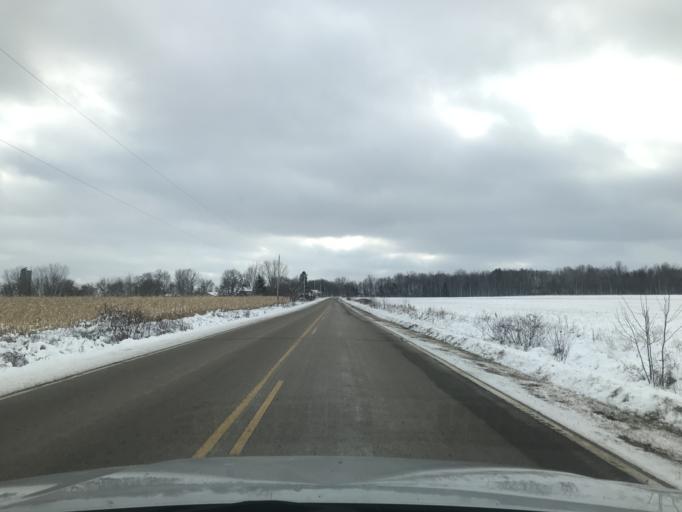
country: US
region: Wisconsin
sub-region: Oconto County
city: Oconto
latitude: 44.9493
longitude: -87.9873
